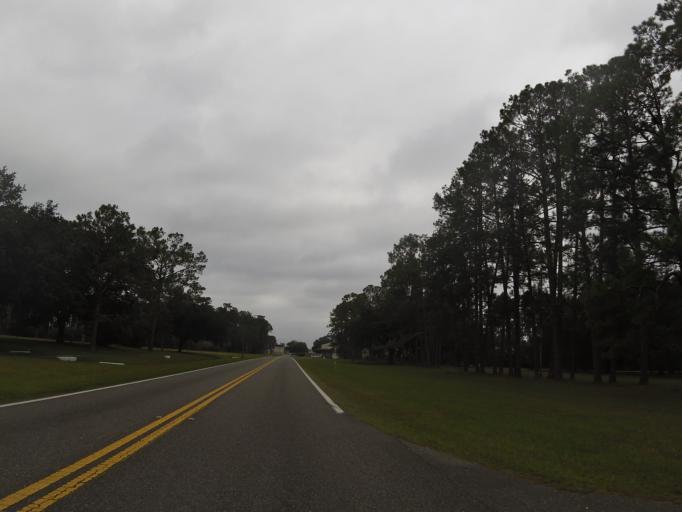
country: US
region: Florida
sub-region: Duval County
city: Baldwin
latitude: 30.2277
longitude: -81.8896
